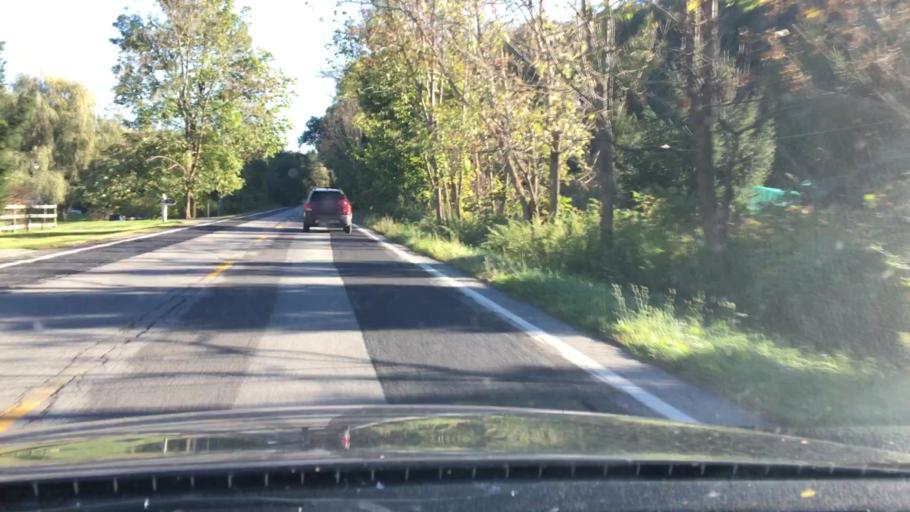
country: US
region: Connecticut
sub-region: Fairfield County
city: Sherman
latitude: 41.6494
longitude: -73.5292
